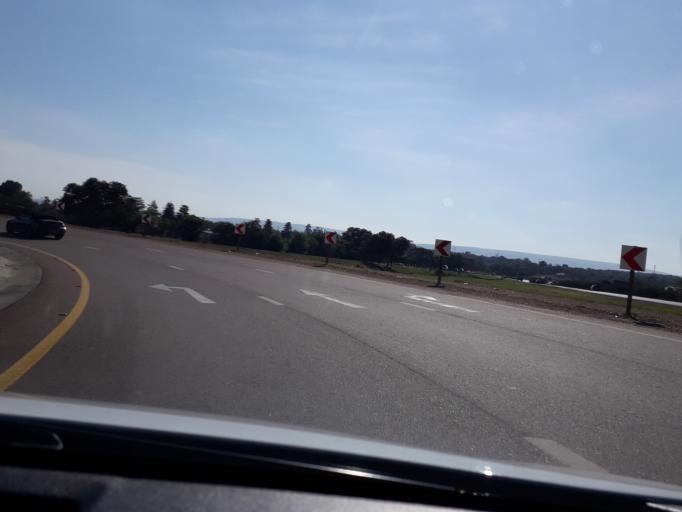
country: ZA
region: Gauteng
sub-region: City of Tshwane Metropolitan Municipality
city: Pretoria
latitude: -25.7518
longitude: 28.3273
